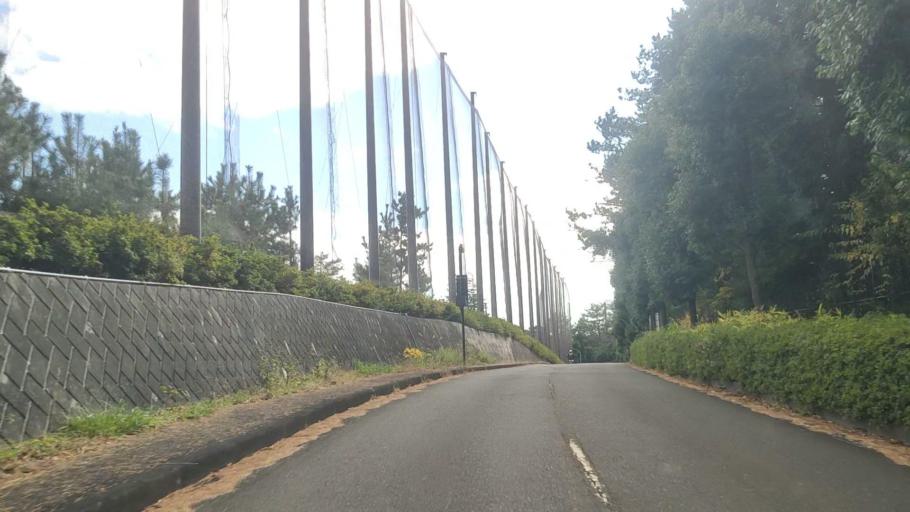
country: JP
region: Kanagawa
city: Yokohama
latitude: 35.4447
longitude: 139.5514
